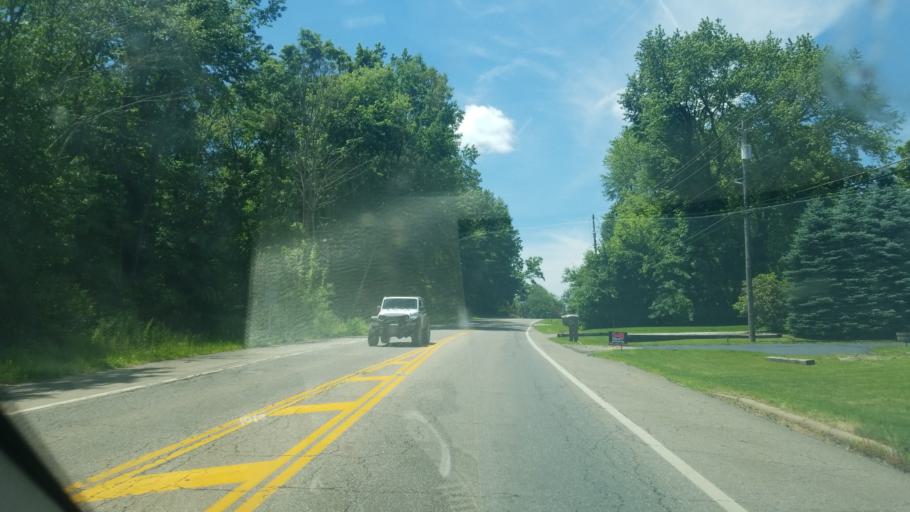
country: US
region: Ohio
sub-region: Columbiana County
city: Salem
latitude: 40.8789
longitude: -80.8588
